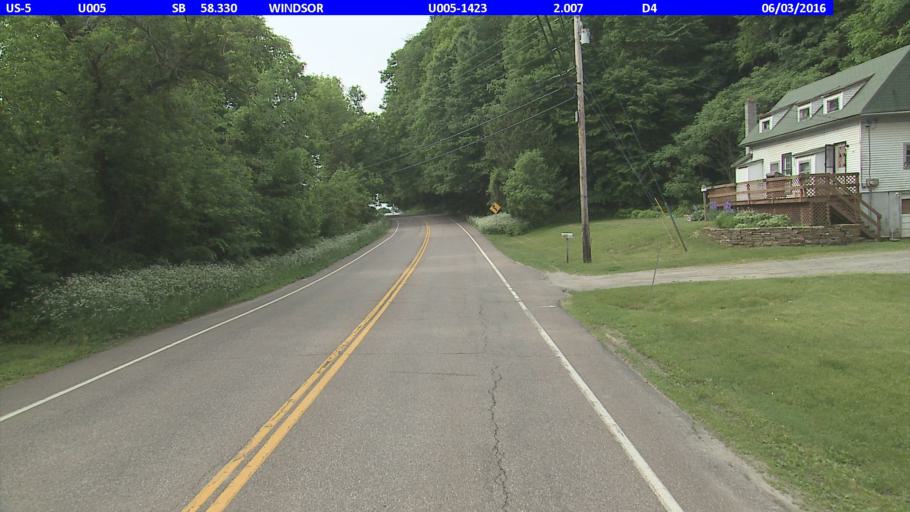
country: US
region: Vermont
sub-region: Windsor County
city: Windsor
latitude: 43.4572
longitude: -72.3944
